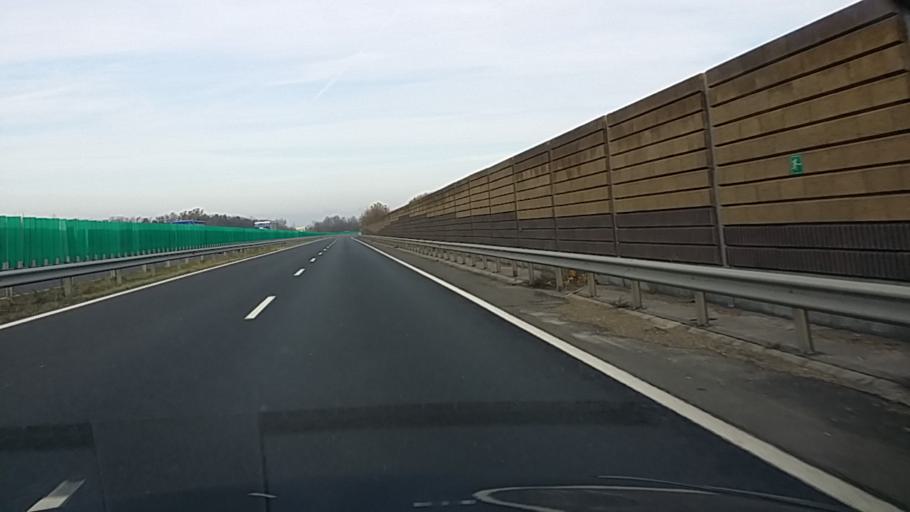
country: HU
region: Fejer
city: Sarszentmihaly
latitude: 47.1592
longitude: 18.3788
